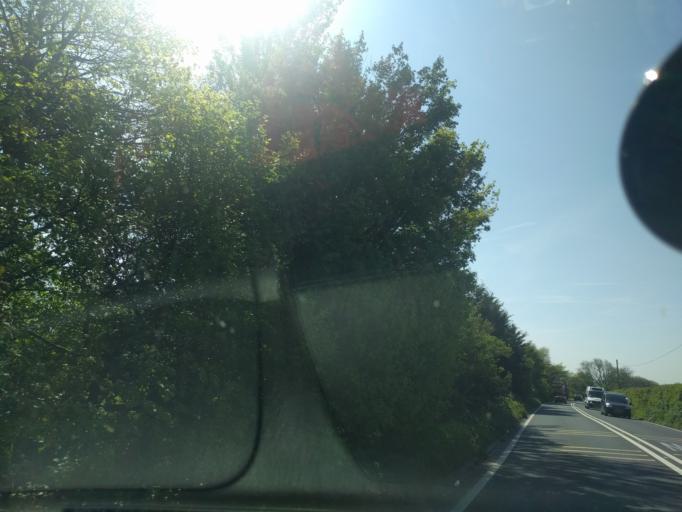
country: GB
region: England
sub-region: Somerset
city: Ilchester
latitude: 51.0576
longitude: -2.6451
